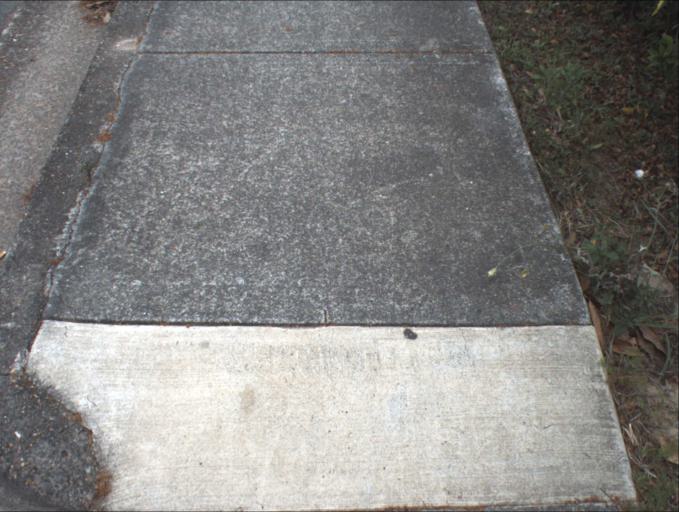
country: AU
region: Queensland
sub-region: Logan
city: Beenleigh
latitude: -27.7205
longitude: 153.2042
